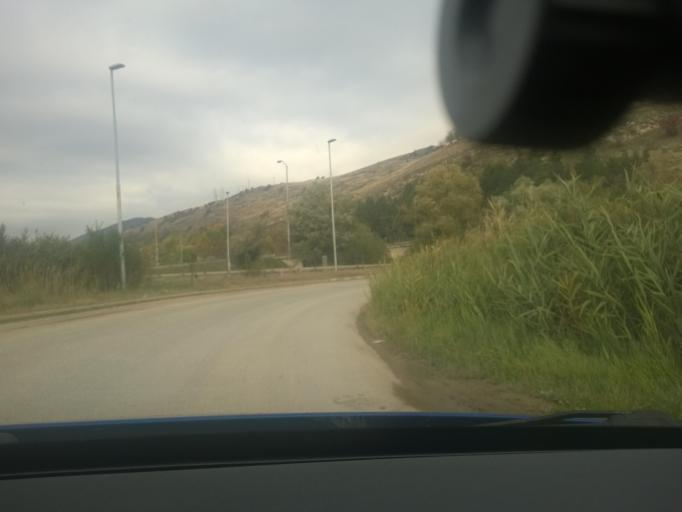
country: RS
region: Central Serbia
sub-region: Pirotski Okrug
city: Pirot
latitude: 43.1582
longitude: 22.5781
